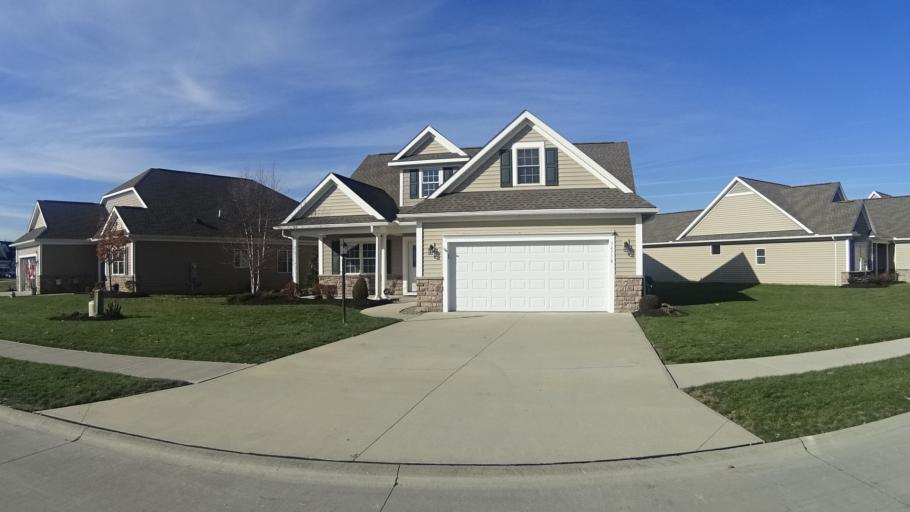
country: US
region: Ohio
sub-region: Lorain County
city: Eaton Estates
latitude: 41.3154
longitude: -81.9937
